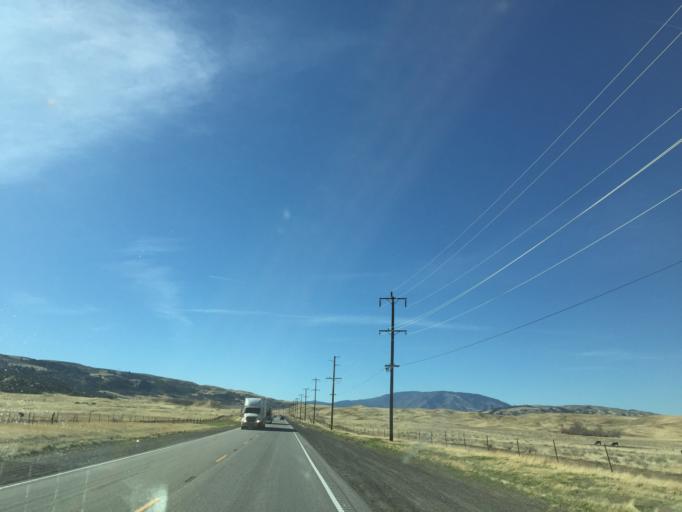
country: US
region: California
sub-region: Kern County
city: Lebec
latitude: 34.7737
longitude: -118.6840
